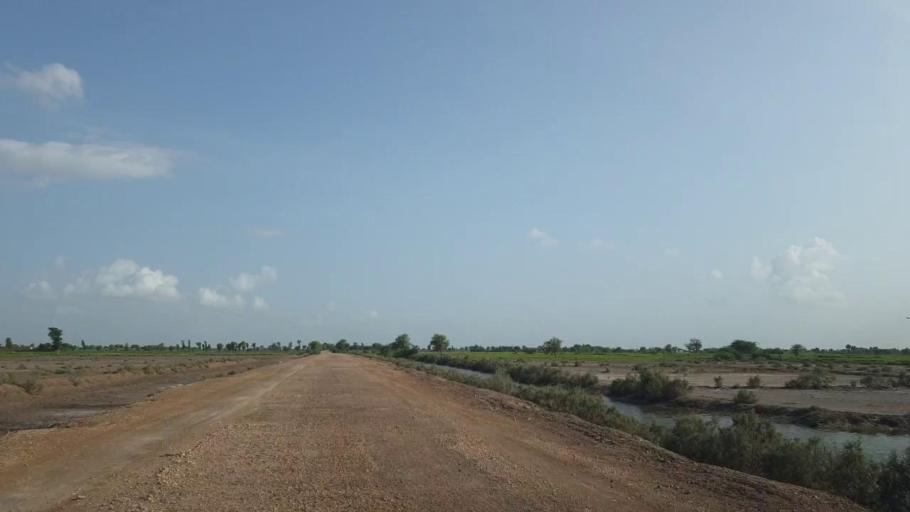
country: PK
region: Sindh
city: Kadhan
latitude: 24.6337
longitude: 69.0960
